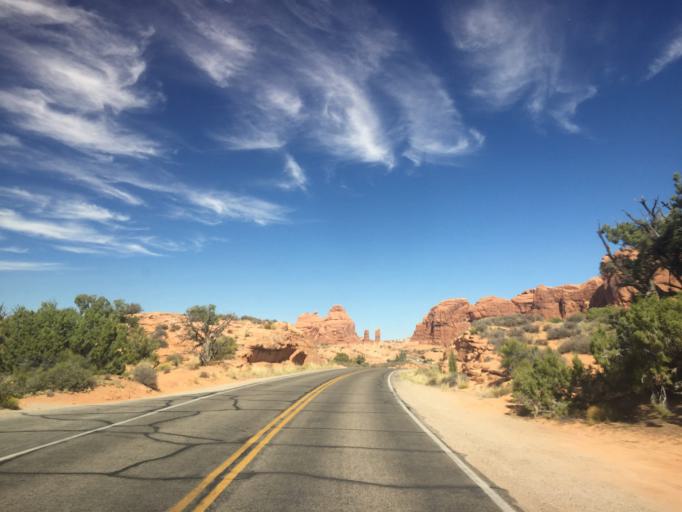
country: US
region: Utah
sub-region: Grand County
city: Moab
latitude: 38.6878
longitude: -109.5424
